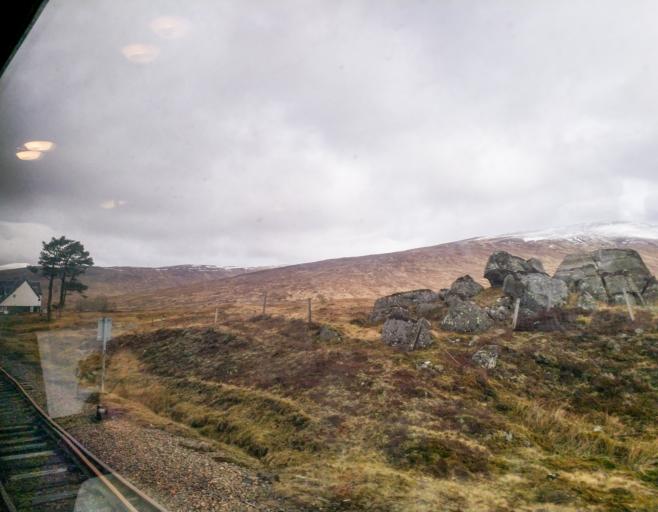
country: GB
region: Scotland
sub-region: Highland
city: Spean Bridge
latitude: 56.7592
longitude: -4.6891
